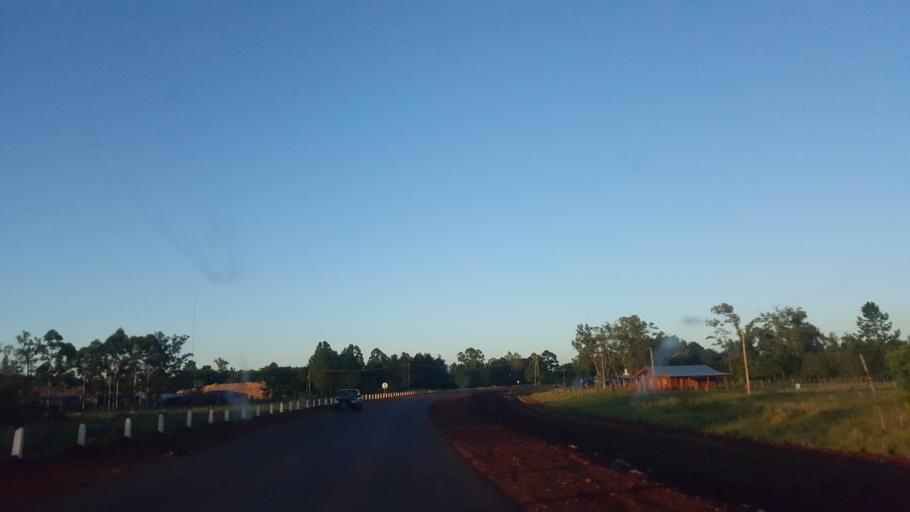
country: AR
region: Corrientes
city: Santo Tome
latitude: -28.5098
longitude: -56.0598
